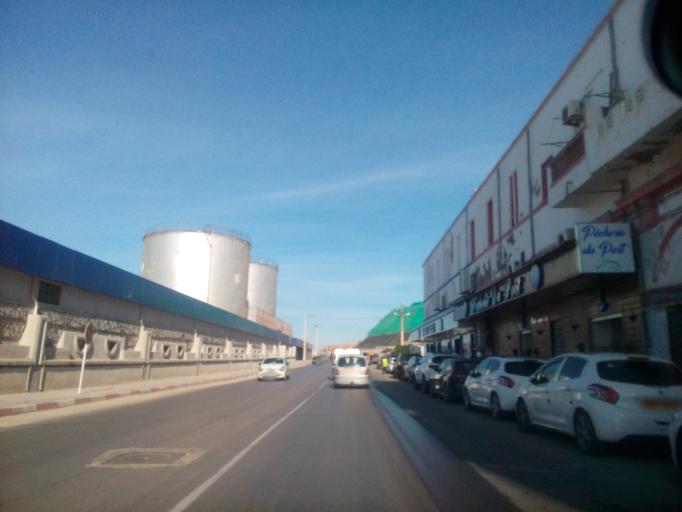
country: DZ
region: Mostaganem
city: Mostaganem
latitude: 35.9374
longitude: 0.0816
